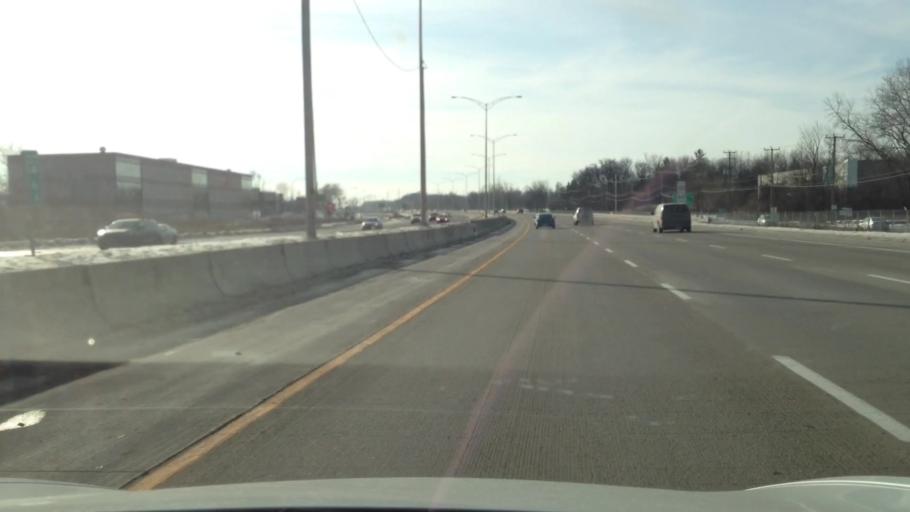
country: CA
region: Quebec
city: Baie-D'Urfe
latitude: 45.4357
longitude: -73.8998
